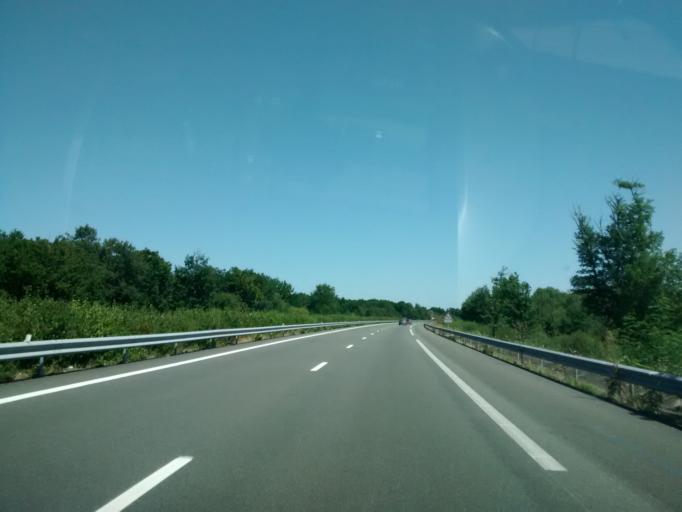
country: FR
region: Aquitaine
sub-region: Departement de la Dordogne
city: Menesplet
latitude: 44.9893
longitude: 0.0952
